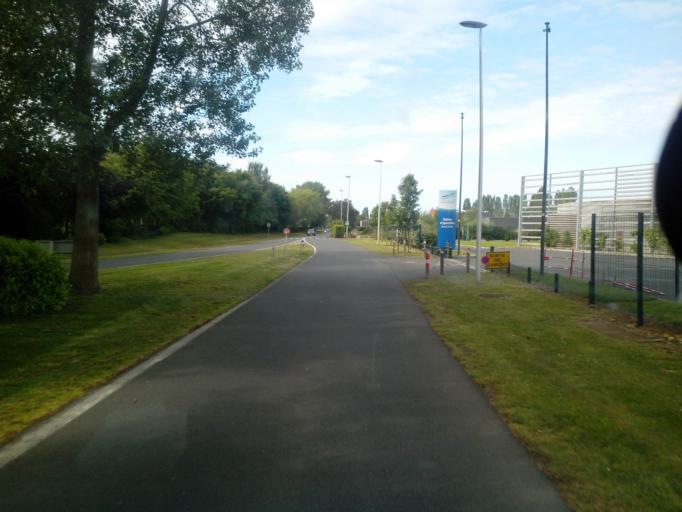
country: FR
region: Lower Normandy
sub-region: Departement du Calvados
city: Cabourg
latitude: 49.2782
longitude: -0.1164
